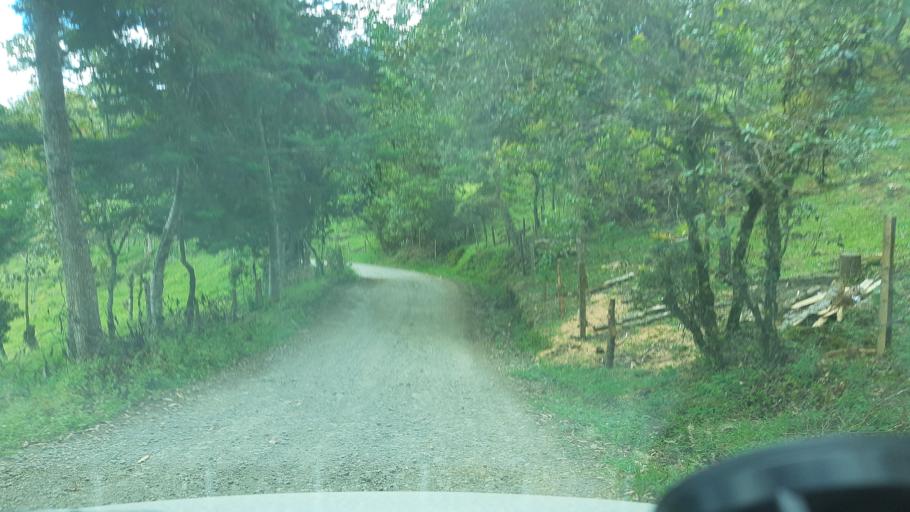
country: CO
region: Boyaca
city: Garagoa
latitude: 5.0493
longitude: -73.3534
